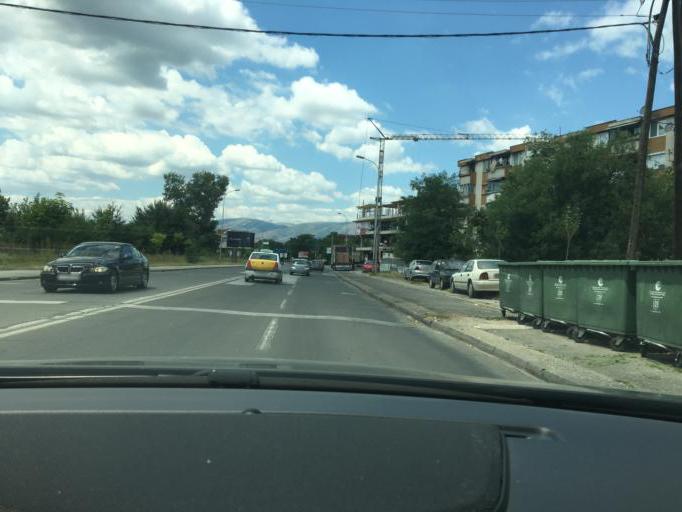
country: MK
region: Saraj
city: Saraj
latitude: 42.0063
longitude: 21.3437
